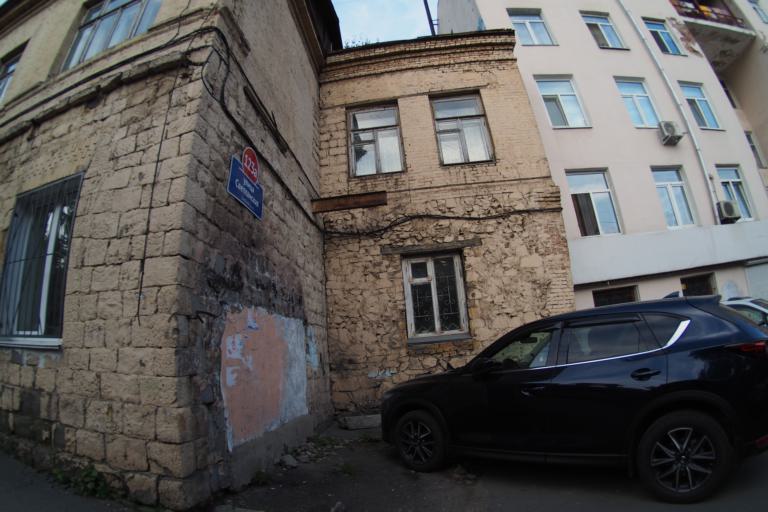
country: RU
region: Primorskiy
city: Vladivostok
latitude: 43.1143
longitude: 131.9118
